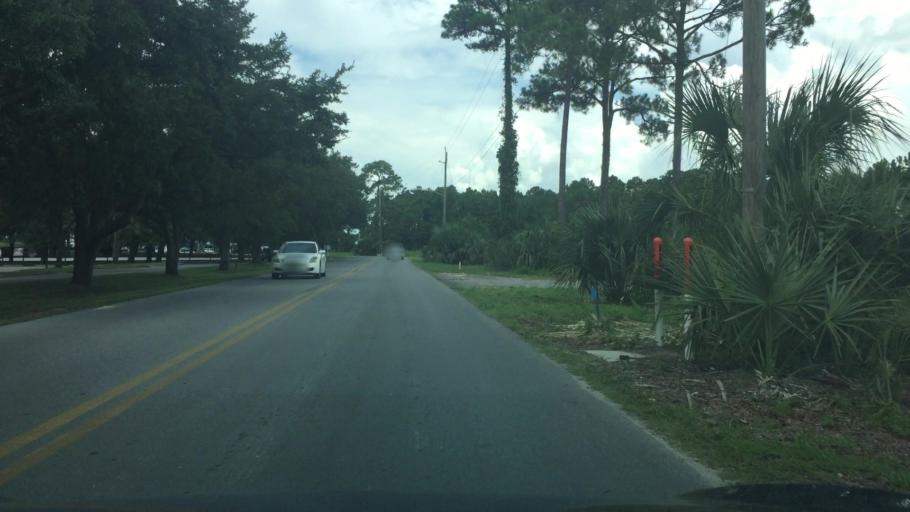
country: US
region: Florida
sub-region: Bay County
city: Lower Grand Lagoon
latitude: 30.1500
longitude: -85.7451
